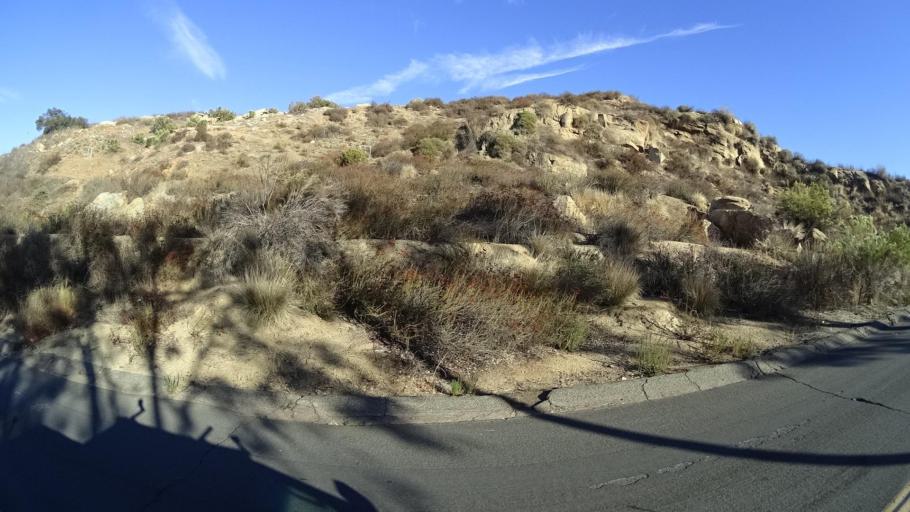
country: US
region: California
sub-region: San Diego County
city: Lakeside
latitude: 32.8410
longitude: -116.9124
